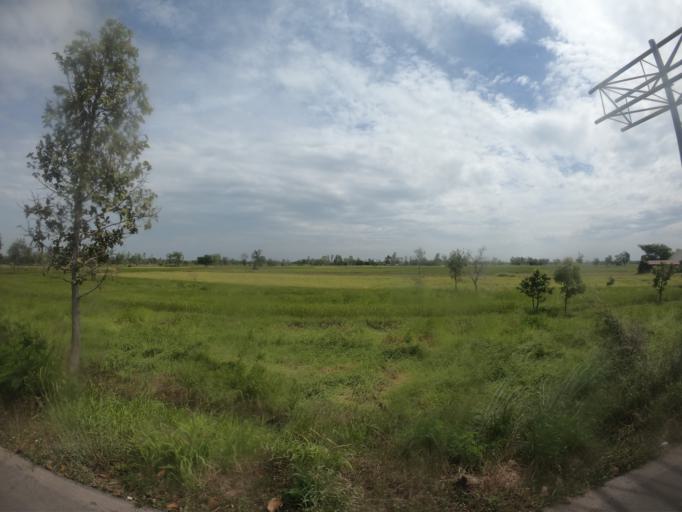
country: TH
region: Maha Sarakham
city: Chiang Yuen
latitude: 16.3747
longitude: 103.1050
